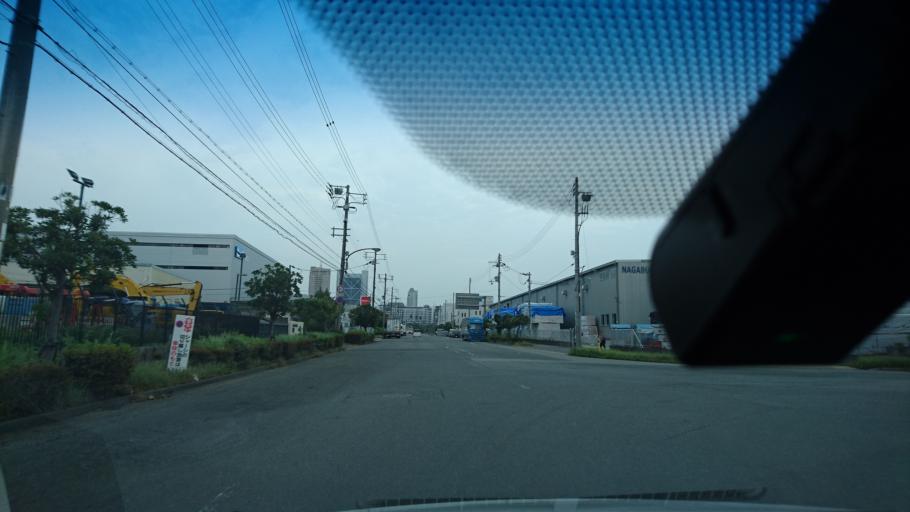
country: JP
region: Hyogo
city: Ashiya
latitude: 34.6879
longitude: 135.2569
